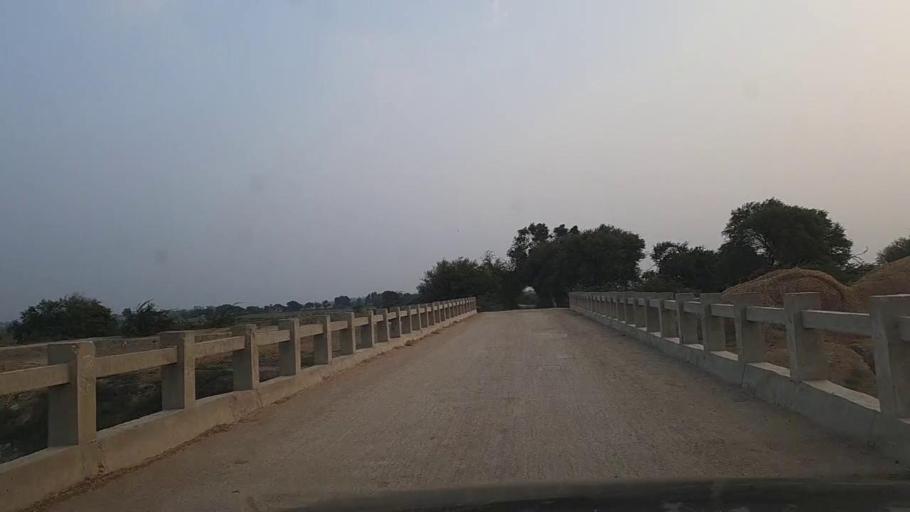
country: PK
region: Sindh
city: Gharo
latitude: 24.7440
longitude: 67.6937
